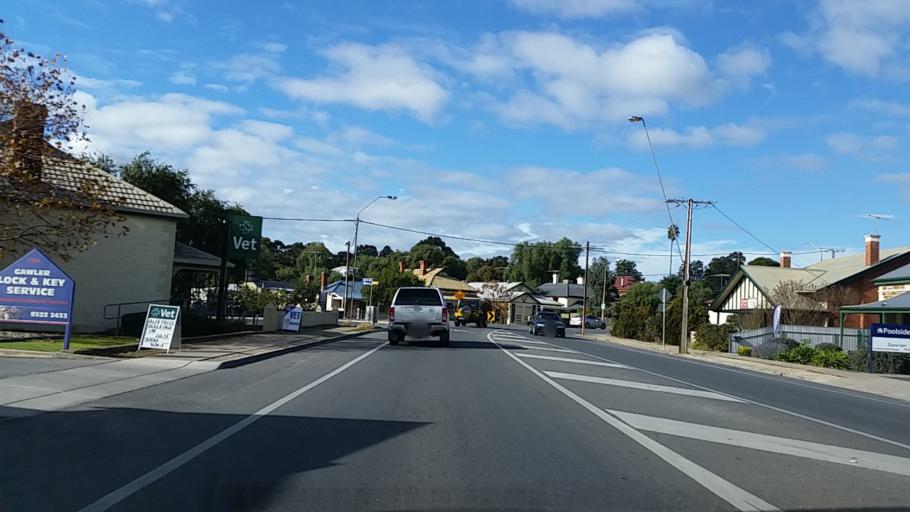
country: AU
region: South Australia
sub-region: Gawler
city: Gawler
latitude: -34.5936
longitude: 138.7484
